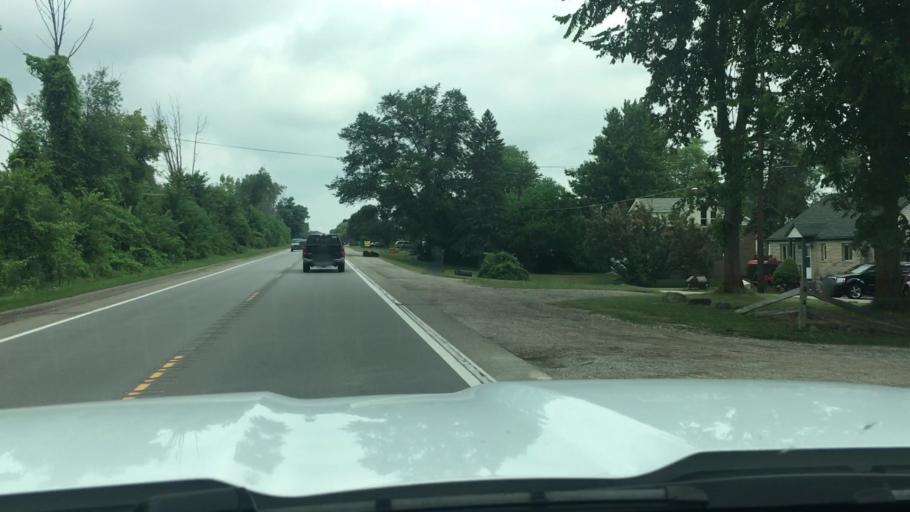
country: US
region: Michigan
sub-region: Lapeer County
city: Imlay City
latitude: 43.0399
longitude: -83.0721
